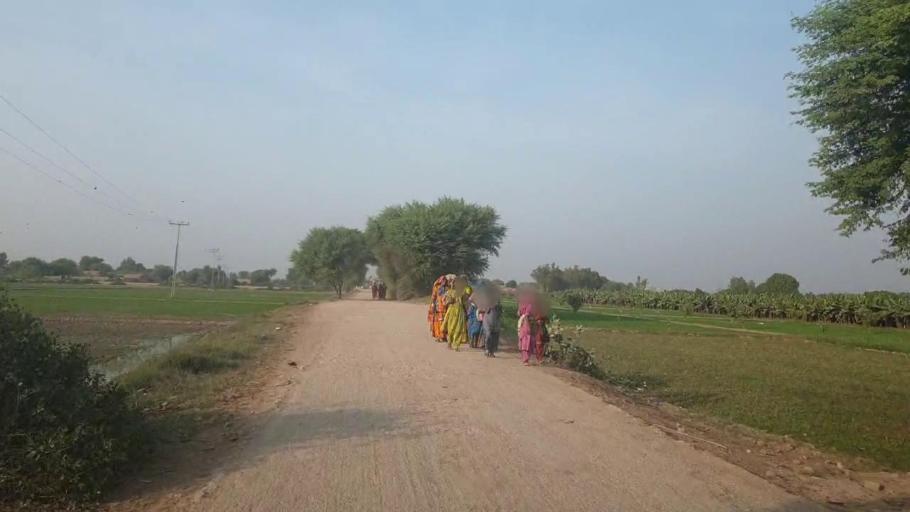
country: PK
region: Sindh
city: Tando Jam
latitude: 25.4379
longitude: 68.5620
